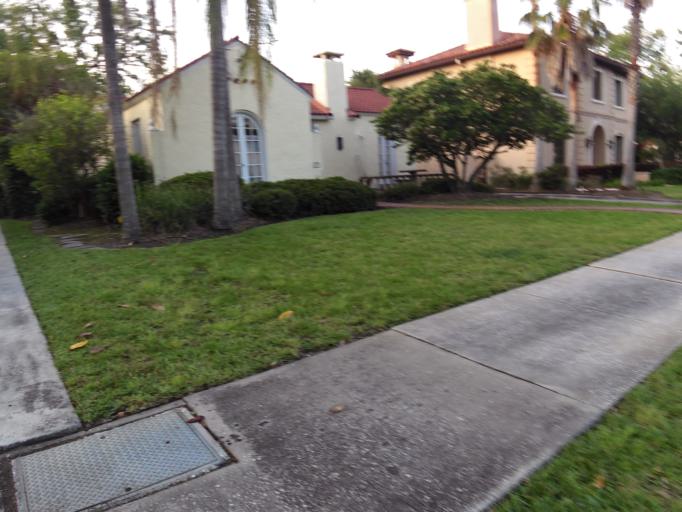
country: US
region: Florida
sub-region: Duval County
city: Jacksonville
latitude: 30.3023
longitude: -81.6547
